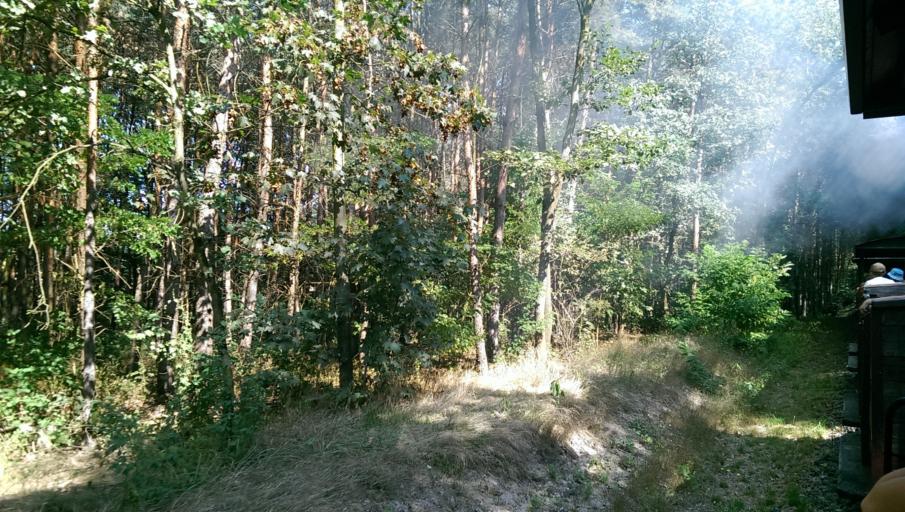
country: CZ
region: Central Bohemia
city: Stary Kolin
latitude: 50.0598
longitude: 15.2688
